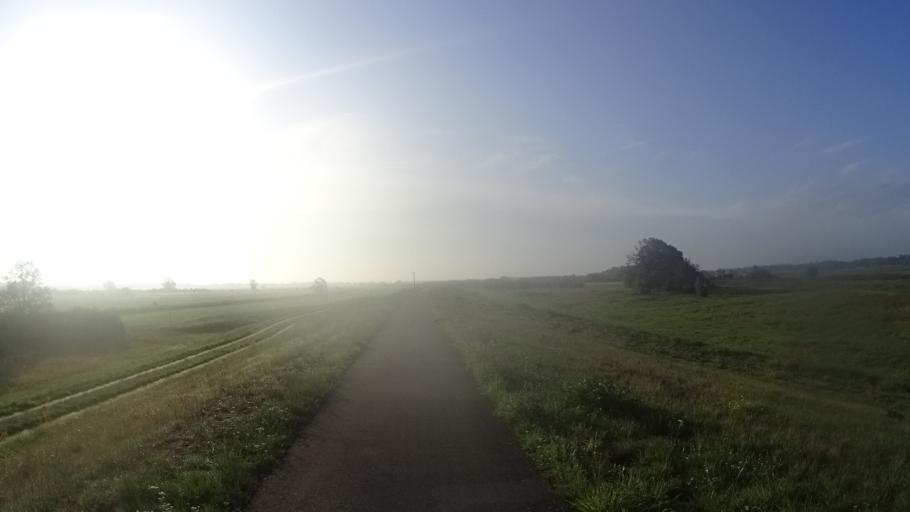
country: DE
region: Brandenburg
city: Lenzen
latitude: 53.0743
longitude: 11.4776
